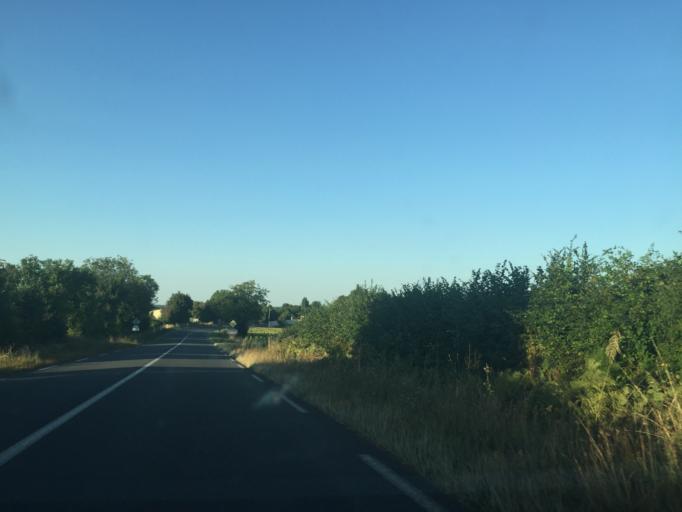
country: FR
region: Poitou-Charentes
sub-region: Departement des Deux-Sevres
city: Lezay
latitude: 46.2961
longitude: -0.0627
